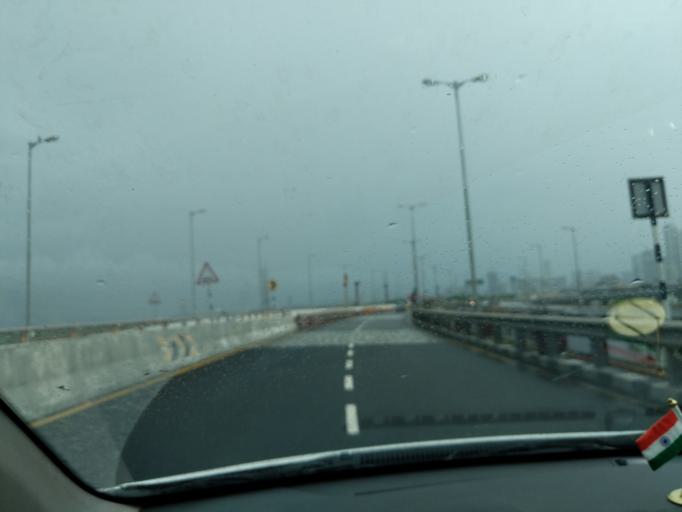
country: IN
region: Maharashtra
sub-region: Mumbai Suburban
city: Mumbai
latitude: 19.0124
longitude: 72.8711
